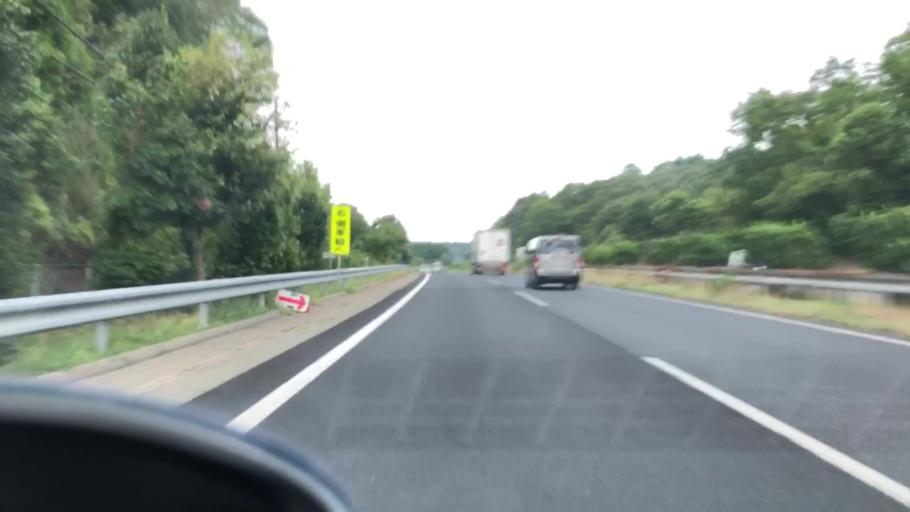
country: JP
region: Hyogo
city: Yashiro
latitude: 34.9148
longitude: 135.0291
